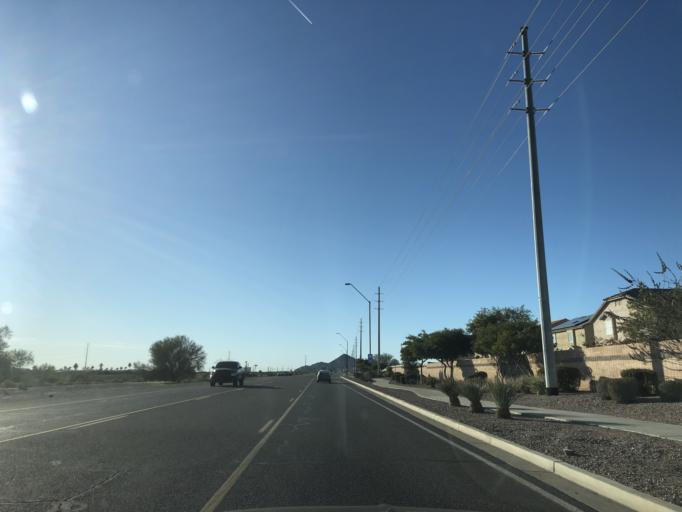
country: US
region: Arizona
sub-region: Maricopa County
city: Buckeye
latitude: 33.4356
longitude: -112.5717
